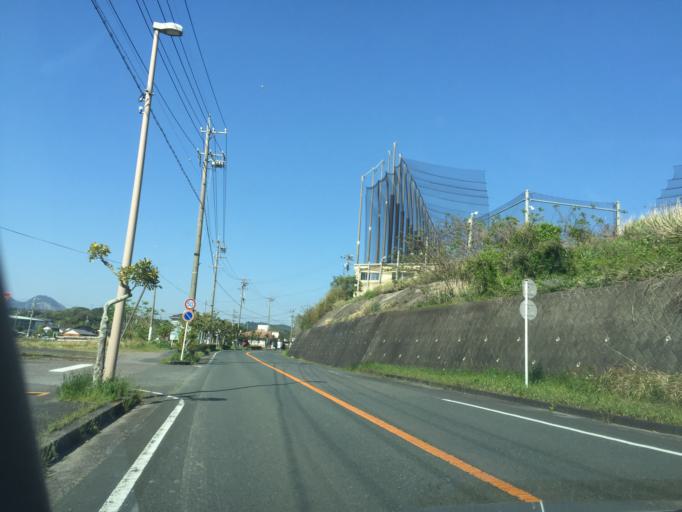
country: JP
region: Shizuoka
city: Kakegawa
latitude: 34.7755
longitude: 138.0349
